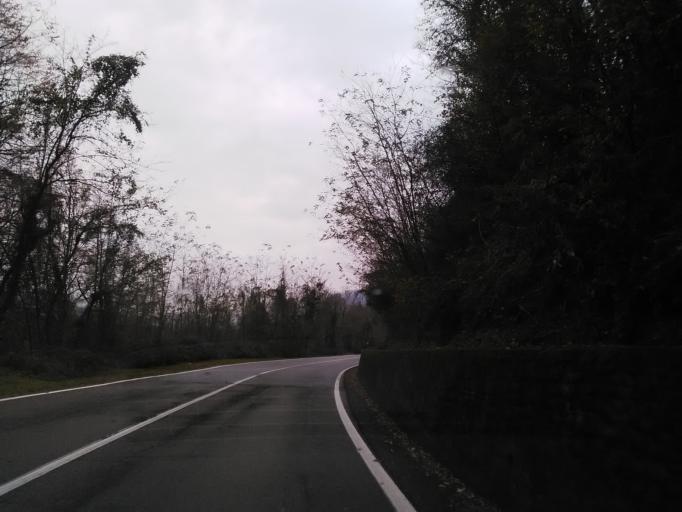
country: IT
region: Piedmont
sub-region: Provincia di Vercelli
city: Quarona
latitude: 45.7758
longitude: 8.2594
